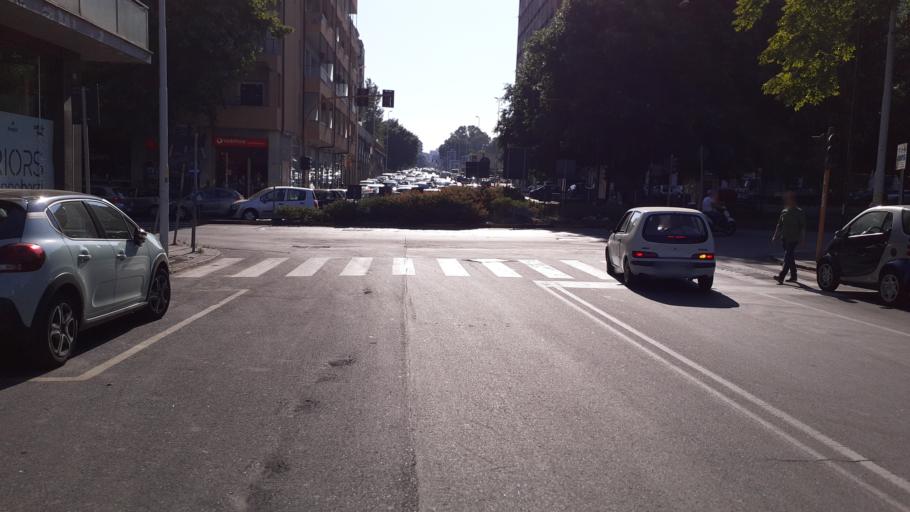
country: IT
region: Sicily
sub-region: Catania
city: Canalicchio
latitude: 37.5225
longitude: 15.0966
